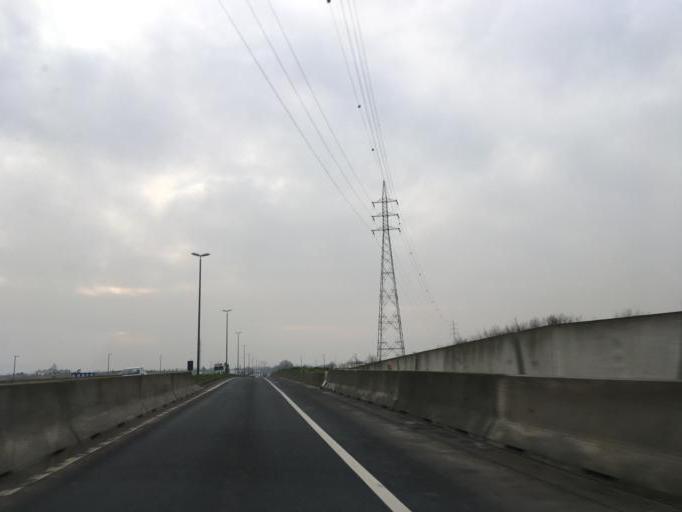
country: BE
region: Flanders
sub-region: Provincie West-Vlaanderen
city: Waregem
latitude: 50.8982
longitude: 3.3981
